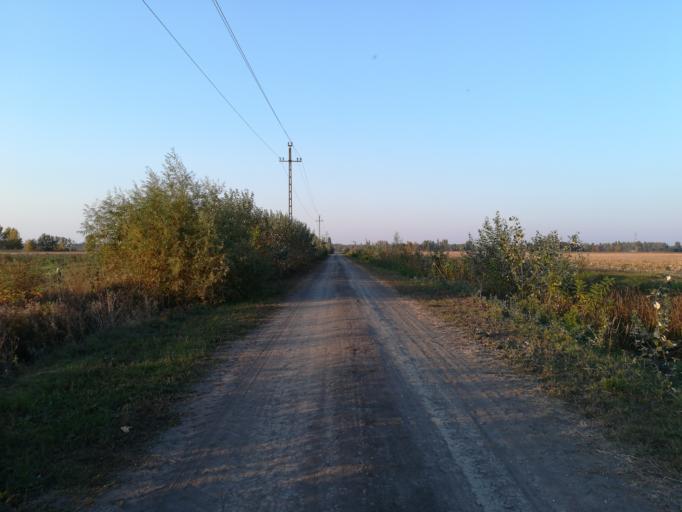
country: HU
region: Bacs-Kiskun
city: Tiszakecske
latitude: 46.9146
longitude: 20.1178
